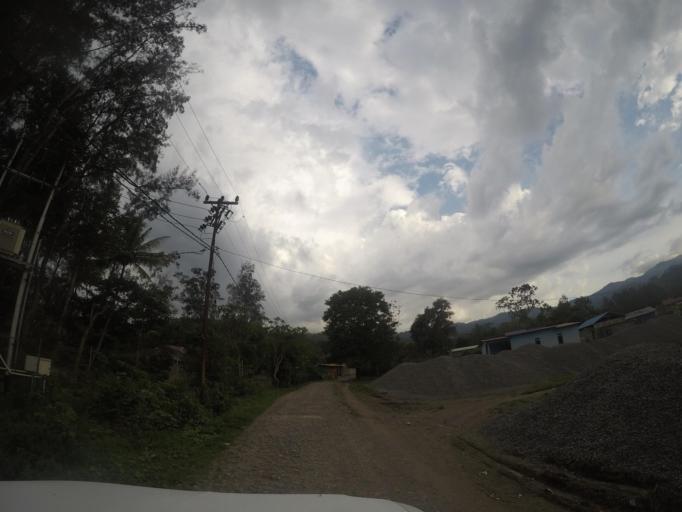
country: TL
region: Ermera
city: Gleno
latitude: -8.7271
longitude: 125.4454
